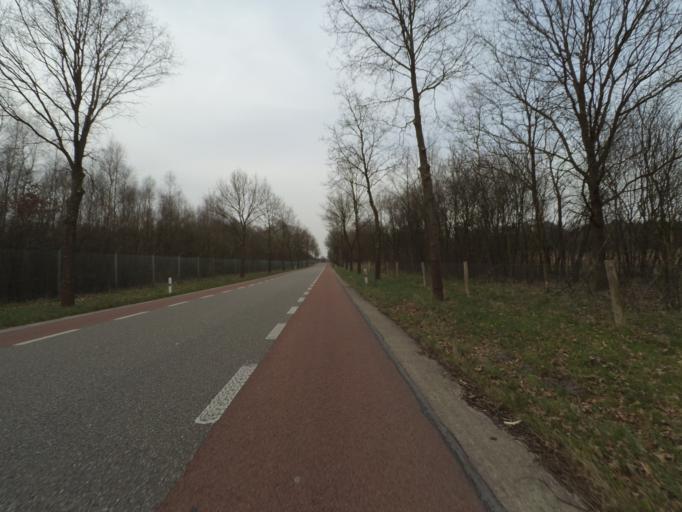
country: NL
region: Gelderland
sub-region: Gemeente Arnhem
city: Gulden Bodem
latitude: 52.0464
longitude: 5.9015
